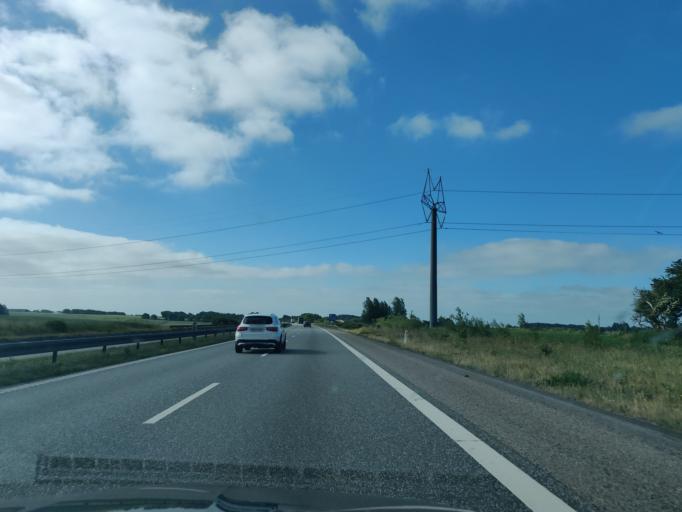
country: DK
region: North Denmark
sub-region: Mariagerfjord Kommune
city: Hobro
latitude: 56.7440
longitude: 9.6980
